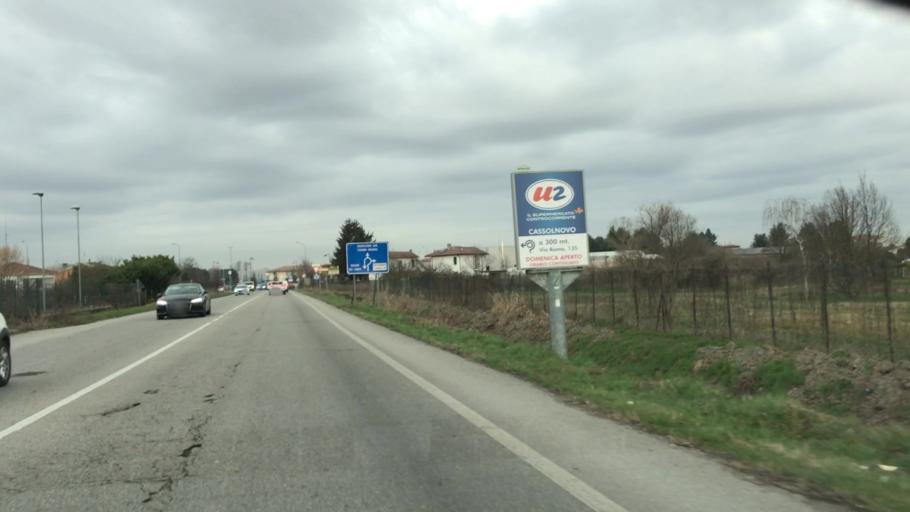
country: IT
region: Lombardy
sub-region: Provincia di Pavia
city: Cassolnovo
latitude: 45.3559
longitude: 8.8170
